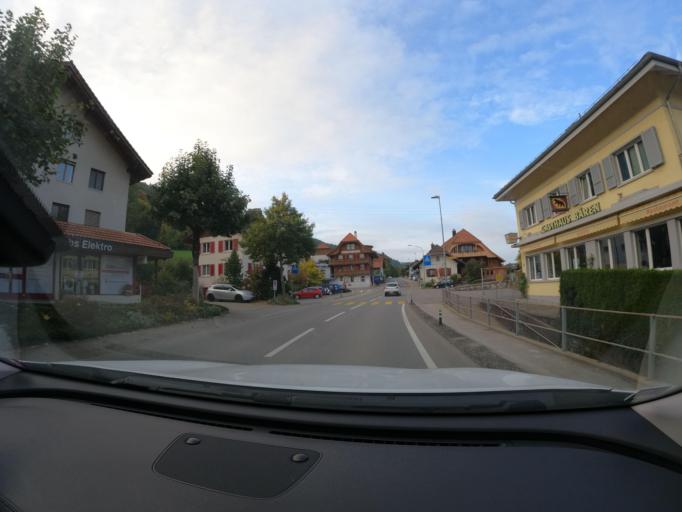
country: CH
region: Bern
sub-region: Bern-Mittelland District
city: Toffen
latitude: 46.8609
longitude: 7.4905
